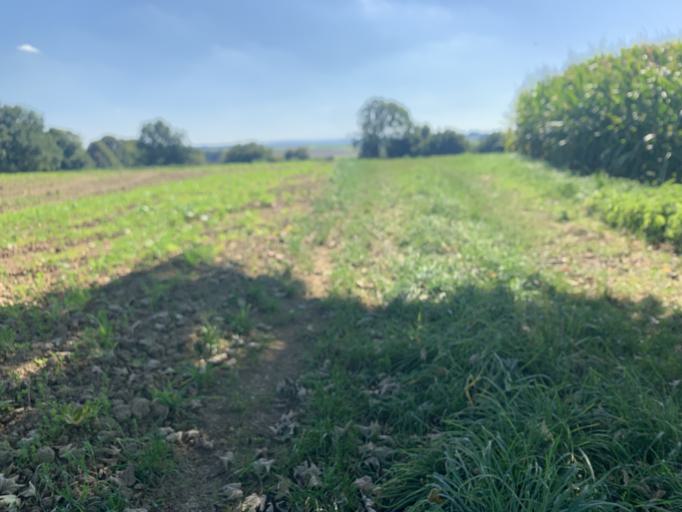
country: DE
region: Bavaria
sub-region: Swabia
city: Mering
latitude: 48.2823
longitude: 11.0053
